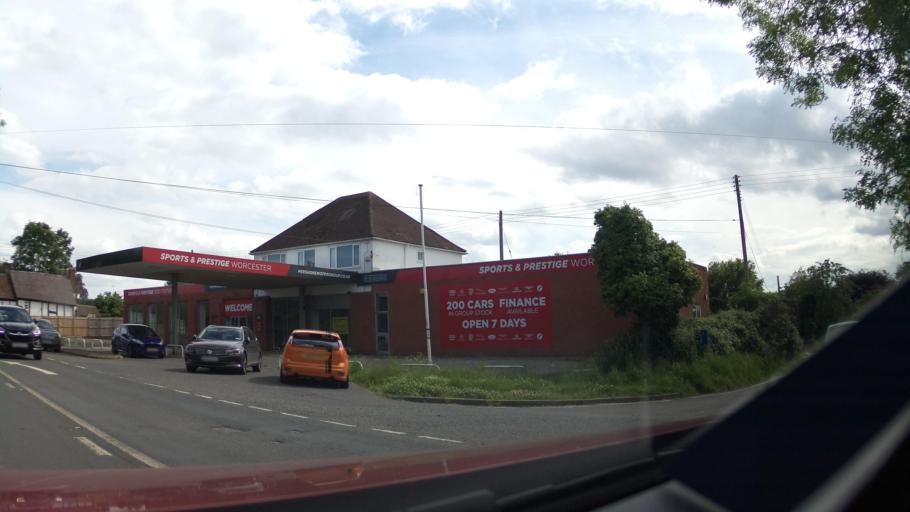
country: GB
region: England
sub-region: Worcestershire
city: Pershore
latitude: 52.1472
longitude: -2.1414
